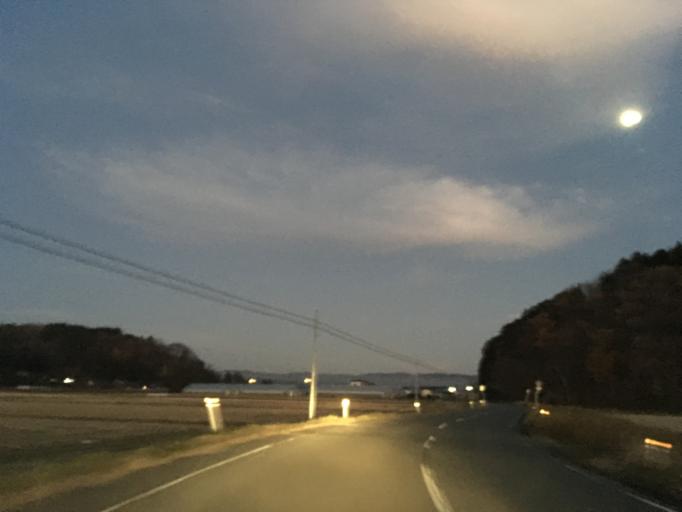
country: JP
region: Iwate
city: Ichinoseki
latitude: 38.7459
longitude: 141.2192
